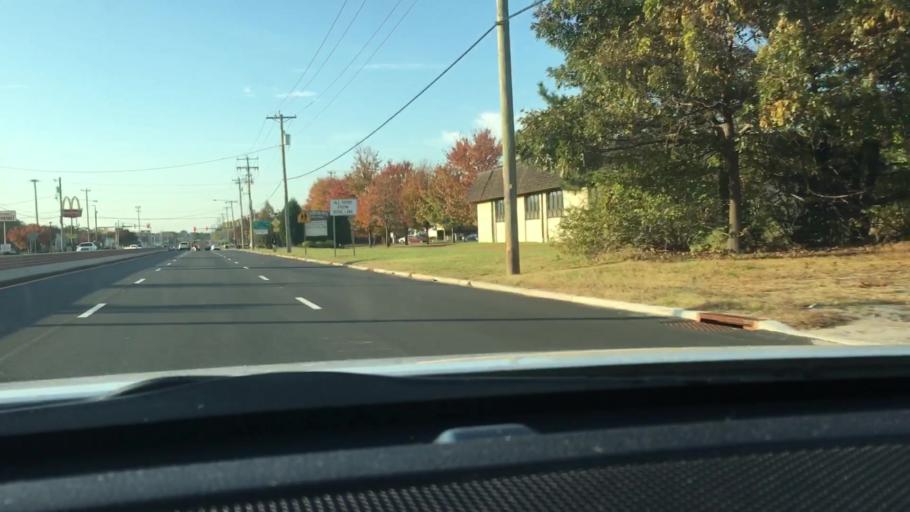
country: US
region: New Jersey
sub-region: Atlantic County
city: Absecon
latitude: 39.4306
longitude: -74.5092
